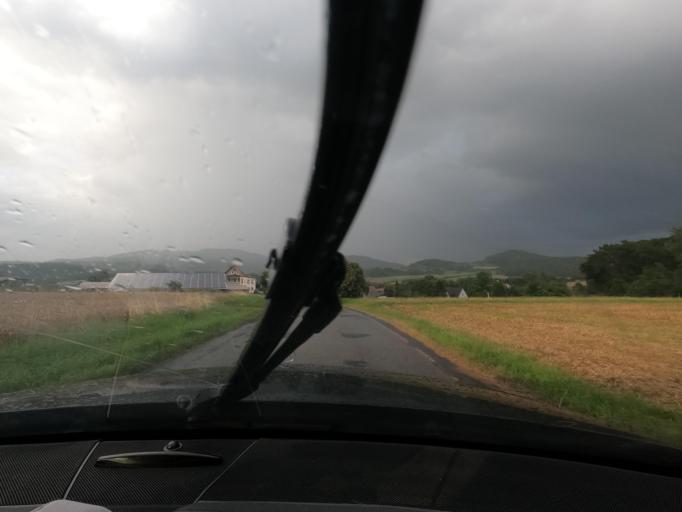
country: DE
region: Hesse
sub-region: Regierungsbezirk Kassel
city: Martinhagen
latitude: 51.3292
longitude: 9.2400
